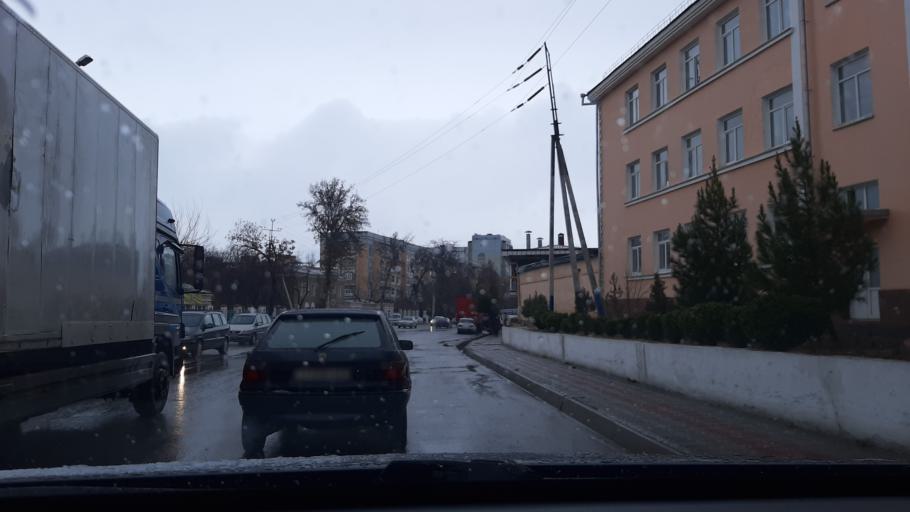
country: TJ
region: Viloyati Sughd
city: Khujand
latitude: 40.2748
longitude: 69.6412
